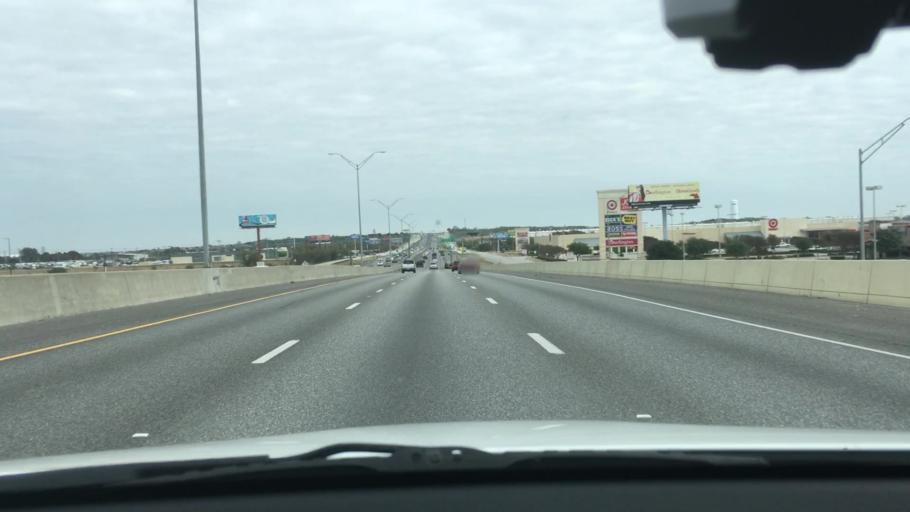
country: US
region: Texas
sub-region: Guadalupe County
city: Lake Dunlap
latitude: 29.7297
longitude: -98.0772
